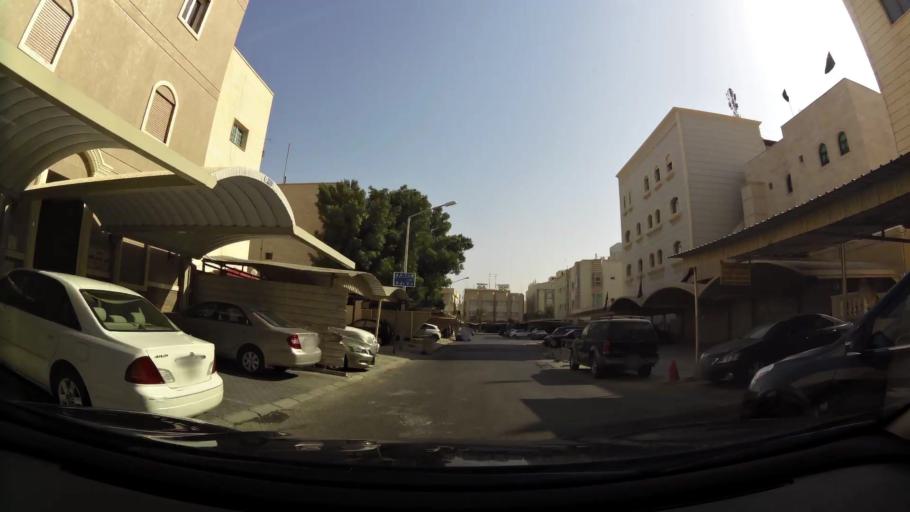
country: KW
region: Muhafazat Hawalli
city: Salwa
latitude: 29.2904
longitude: 48.0774
